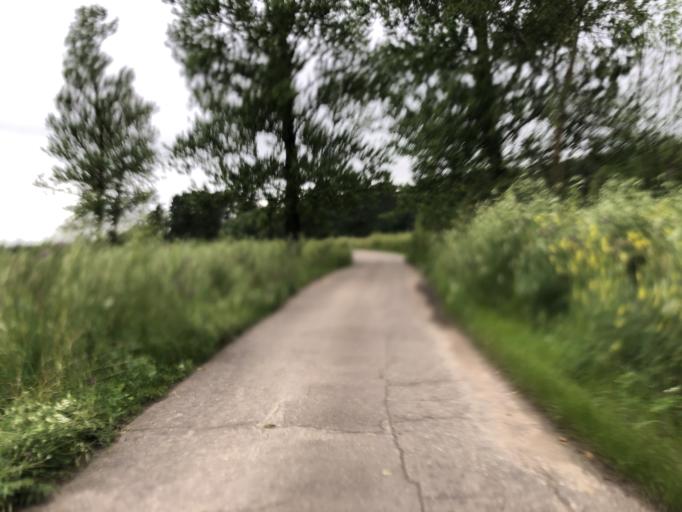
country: RU
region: Tverskaya
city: Rzhev
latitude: 56.2447
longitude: 34.3723
